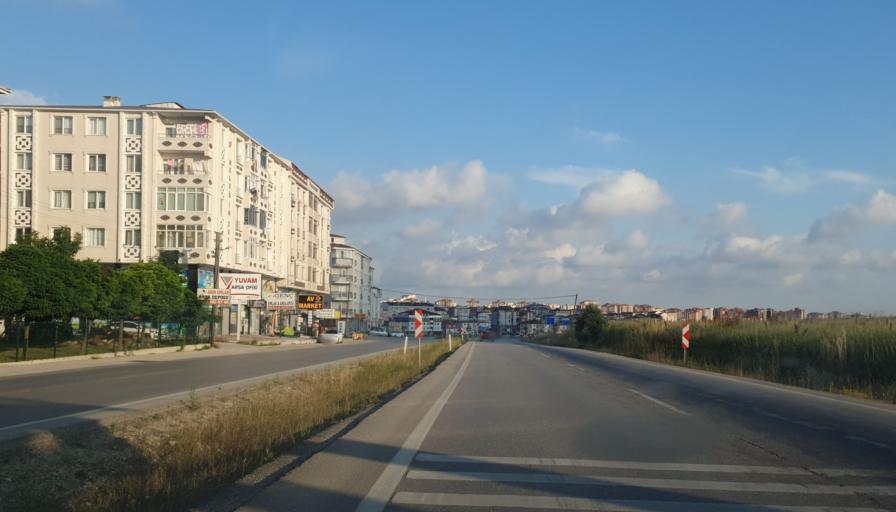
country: TR
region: Tekirdag
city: Cerkezkoey
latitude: 41.3345
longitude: 27.9685
